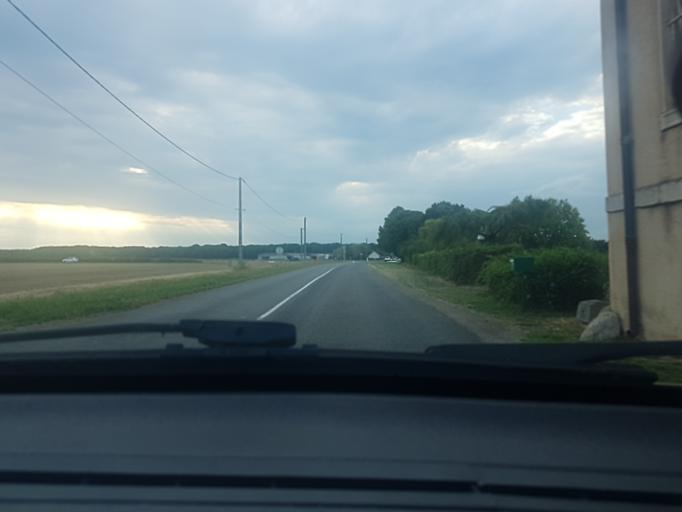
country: FR
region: Bourgogne
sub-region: Departement de Saone-et-Loire
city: Sennecey-le-Grand
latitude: 46.6707
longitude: 4.8152
